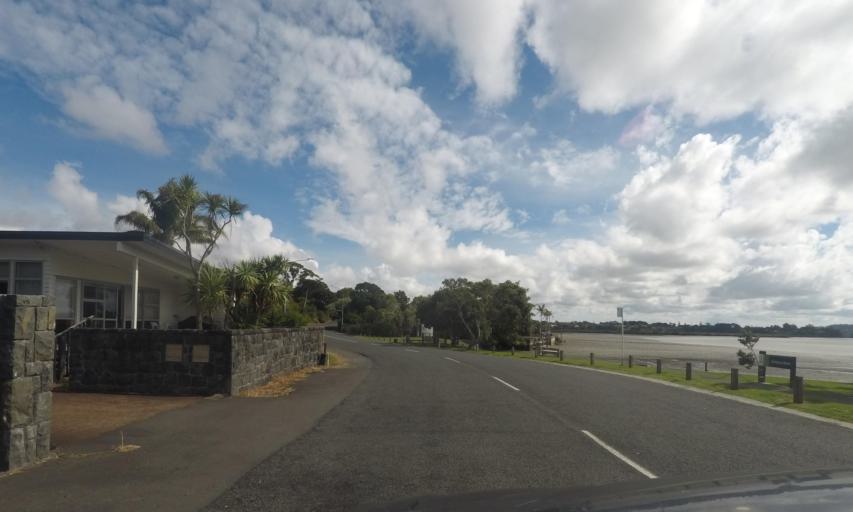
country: NZ
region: Auckland
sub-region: Auckland
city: North Shore
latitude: -36.7773
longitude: 174.6591
